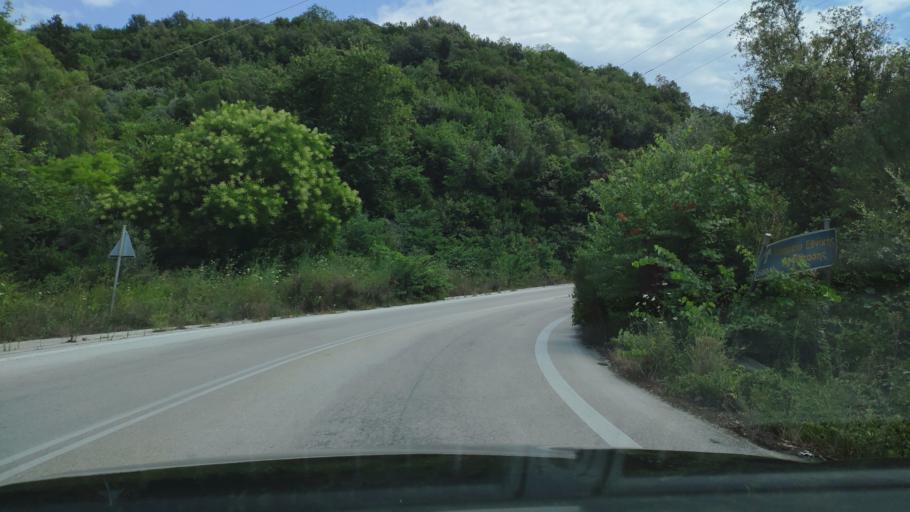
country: GR
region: West Greece
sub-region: Nomos Aitolias kai Akarnanias
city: Menidi
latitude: 39.0260
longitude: 21.1328
